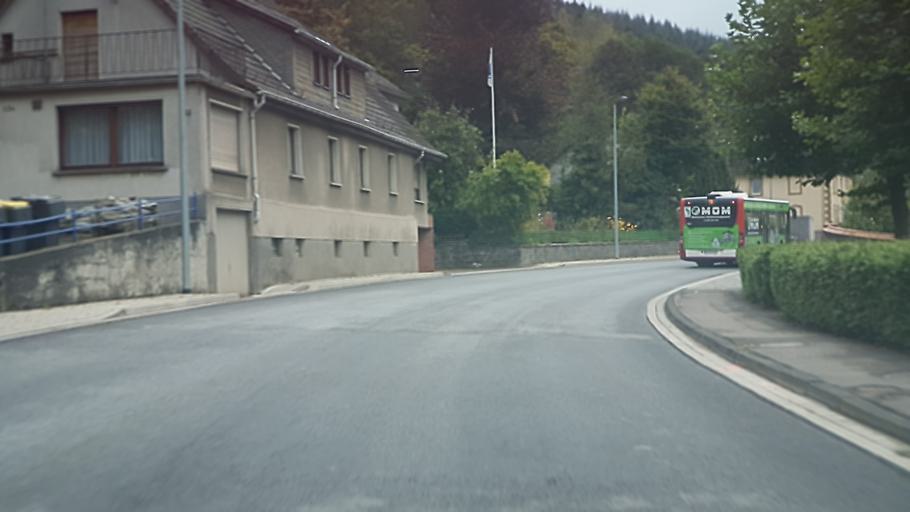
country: DE
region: North Rhine-Westphalia
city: Plettenberg
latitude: 51.1737
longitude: 7.8610
